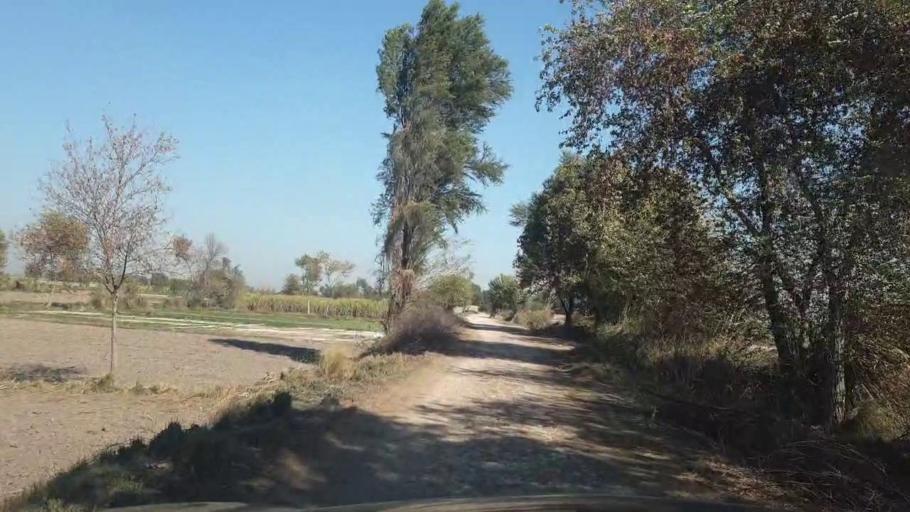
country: PK
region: Sindh
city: Ghotki
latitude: 27.9785
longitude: 69.4205
